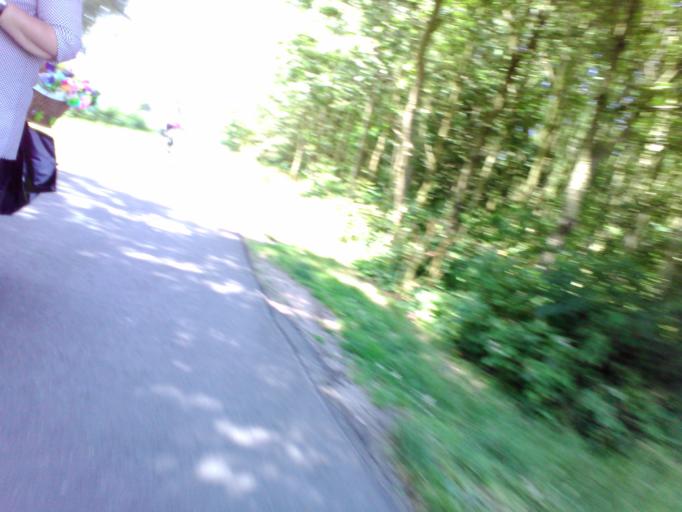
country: NL
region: South Holland
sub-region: Gemeente Westland
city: De Lier
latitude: 51.9688
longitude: 4.2755
